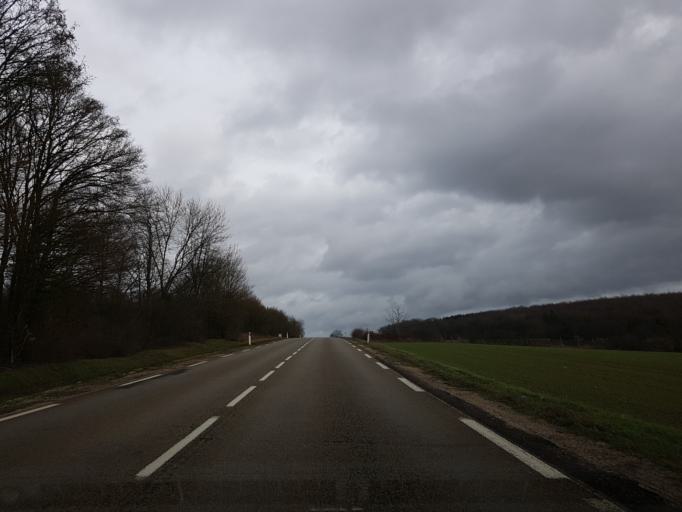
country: FR
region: Franche-Comte
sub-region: Departement de la Haute-Saone
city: Jussey
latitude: 47.7209
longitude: 5.8496
